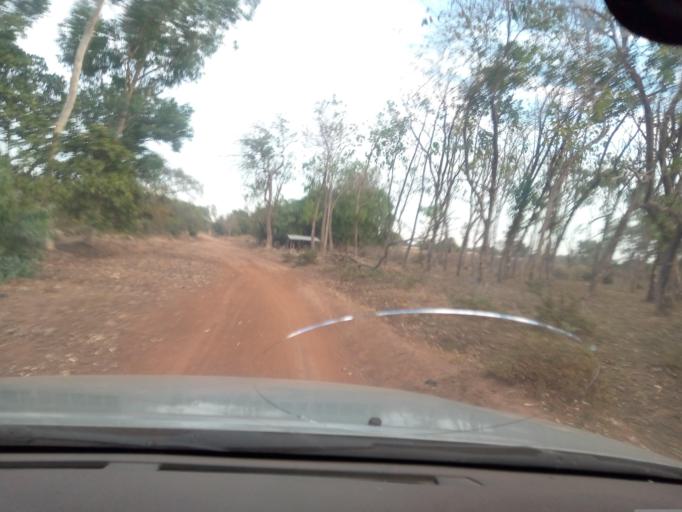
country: ML
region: Sikasso
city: Kadiolo
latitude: 10.5809
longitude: -5.8390
